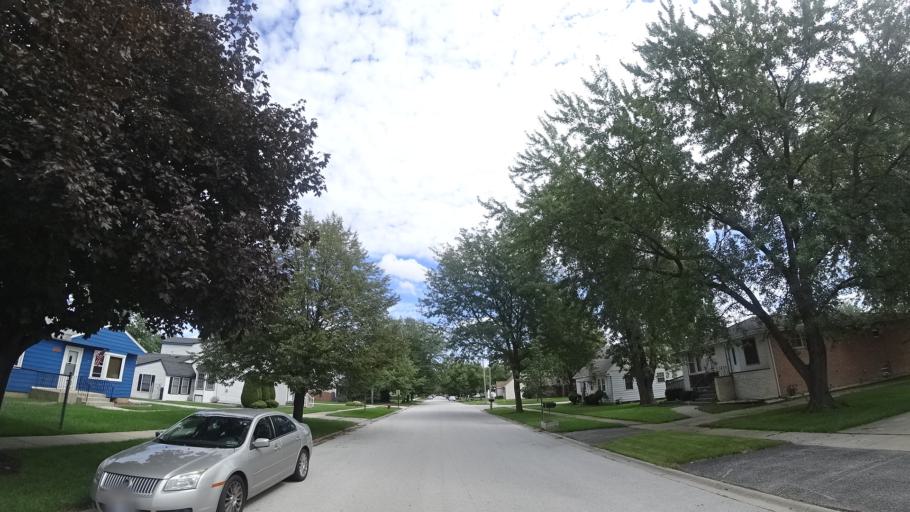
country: US
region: Illinois
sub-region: Cook County
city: Burbank
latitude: 41.7184
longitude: -87.7947
